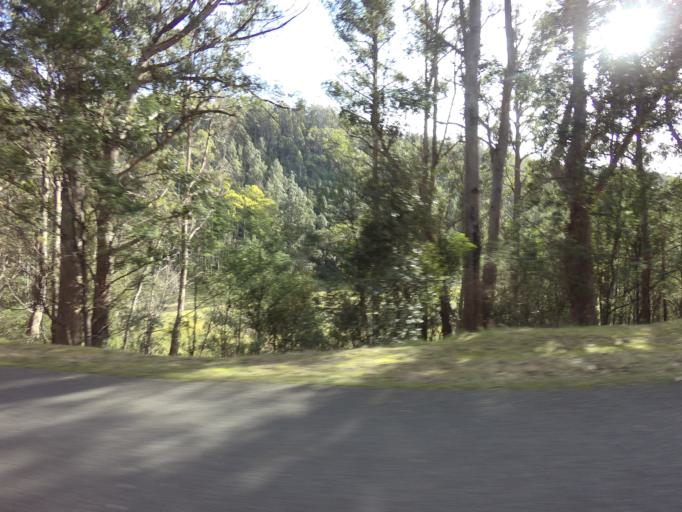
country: AU
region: Tasmania
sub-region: Huon Valley
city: Huonville
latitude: -43.0389
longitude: 147.1370
